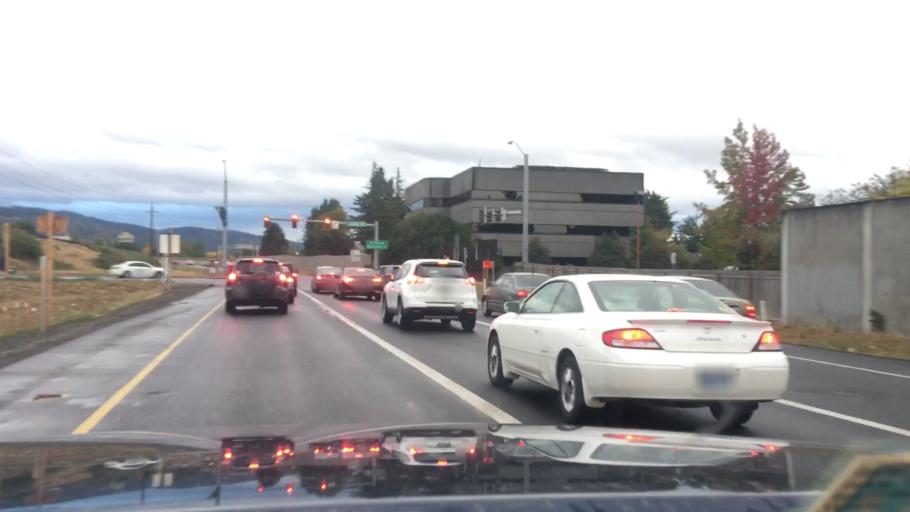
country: US
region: Oregon
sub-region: Lane County
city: Eugene
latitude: 44.0870
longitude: -123.0687
